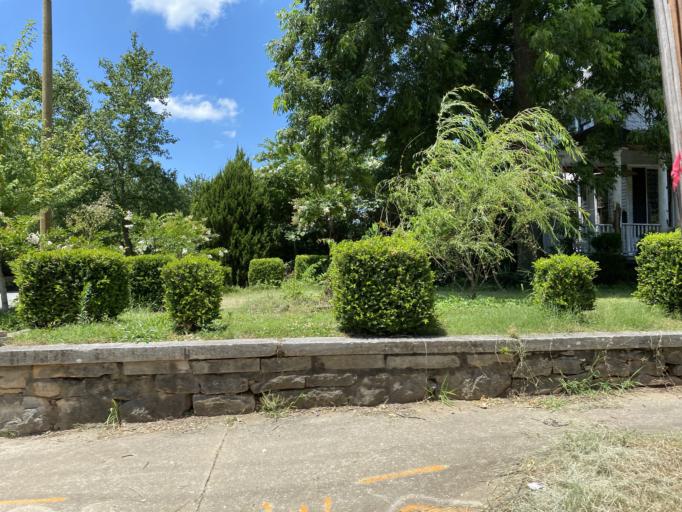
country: US
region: Alabama
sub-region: Morgan County
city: Decatur
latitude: 34.5998
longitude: -86.9802
